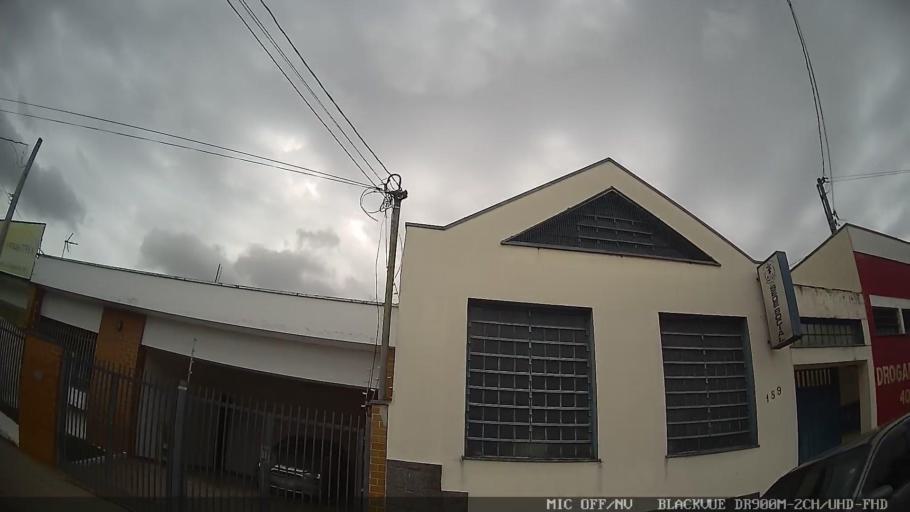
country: BR
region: Sao Paulo
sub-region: Salto
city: Salto
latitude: -23.2081
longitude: -47.2914
